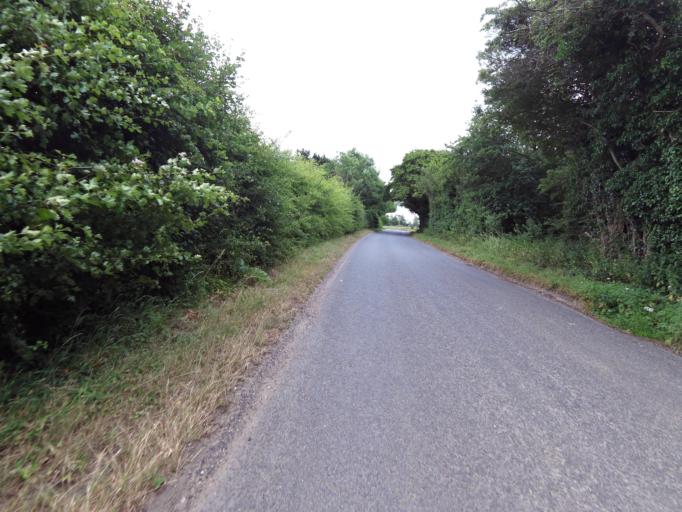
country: GB
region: England
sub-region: Norfolk
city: Harleston
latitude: 52.3979
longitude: 1.2441
